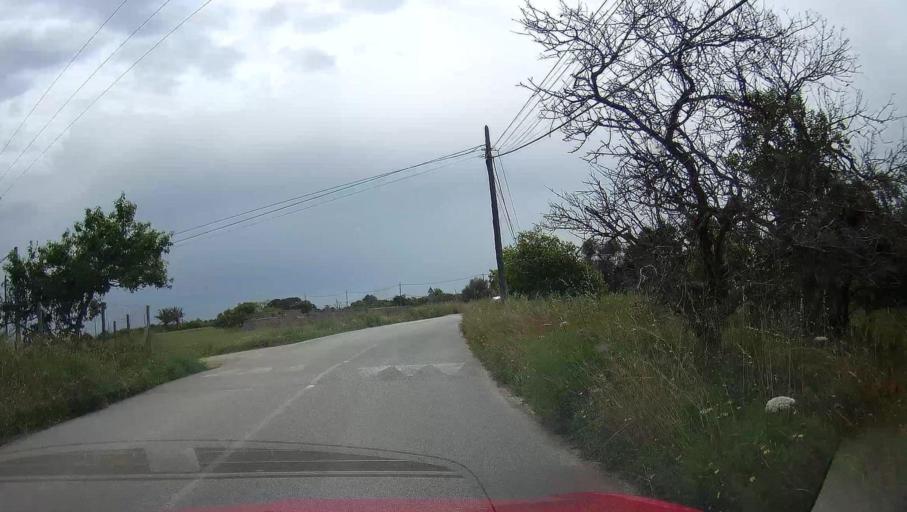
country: ES
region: Balearic Islands
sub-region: Illes Balears
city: Ibiza
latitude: 38.8792
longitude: 1.3595
